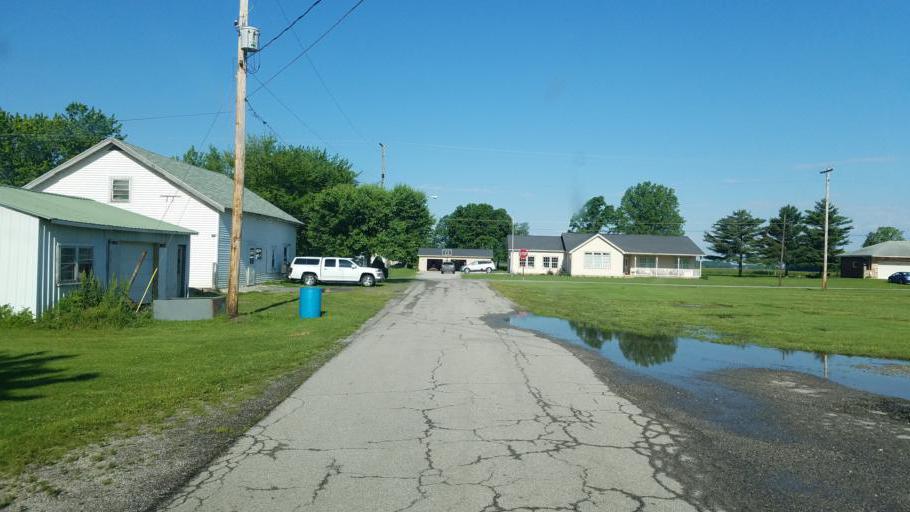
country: US
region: Ohio
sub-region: Union County
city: Richwood
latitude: 40.5874
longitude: -83.3140
